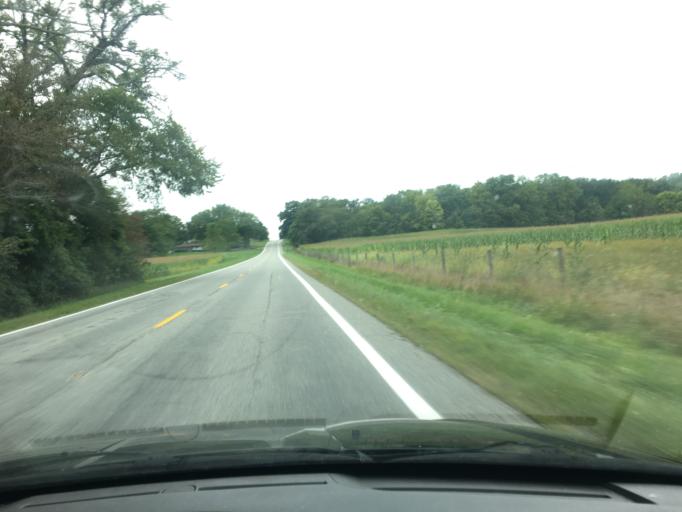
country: US
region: Ohio
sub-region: Champaign County
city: Urbana
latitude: 40.1522
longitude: -83.7018
